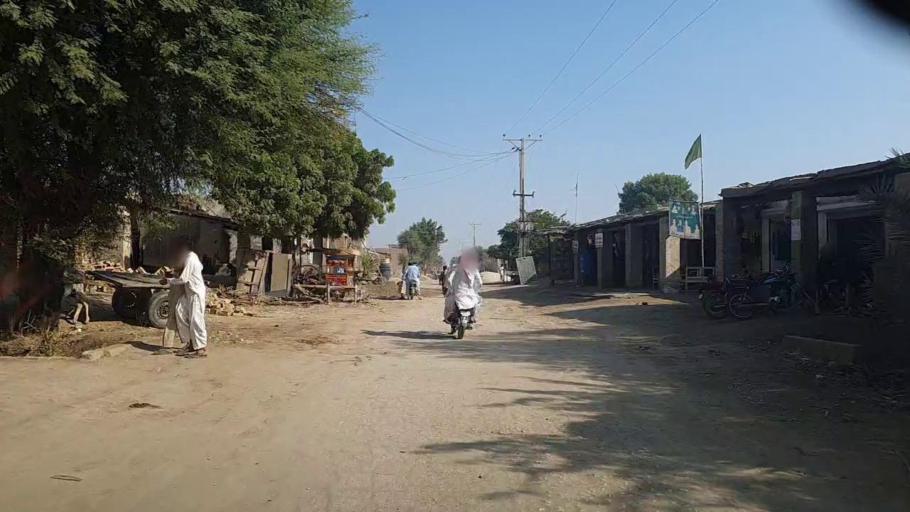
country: PK
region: Sindh
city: Darya Khan Marri
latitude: 26.6741
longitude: 68.3119
